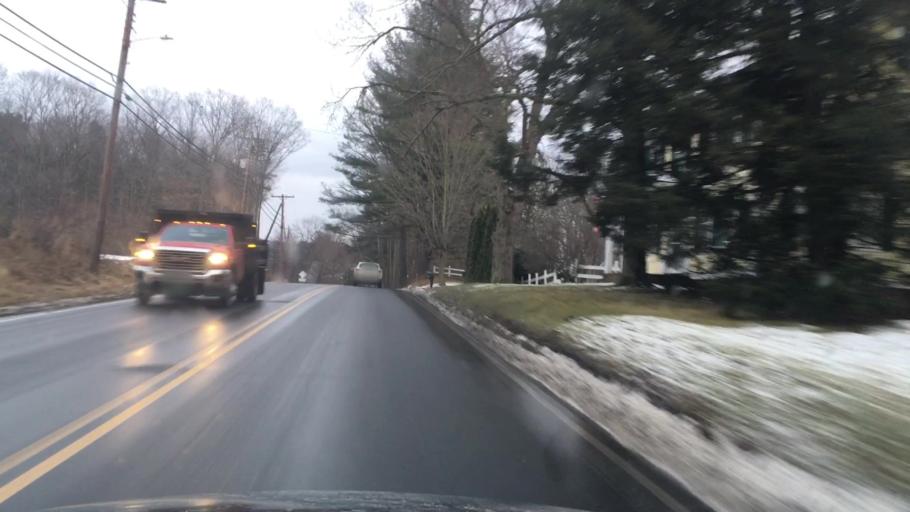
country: US
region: New Hampshire
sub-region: Sullivan County
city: Claremont
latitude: 43.3923
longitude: -72.3757
